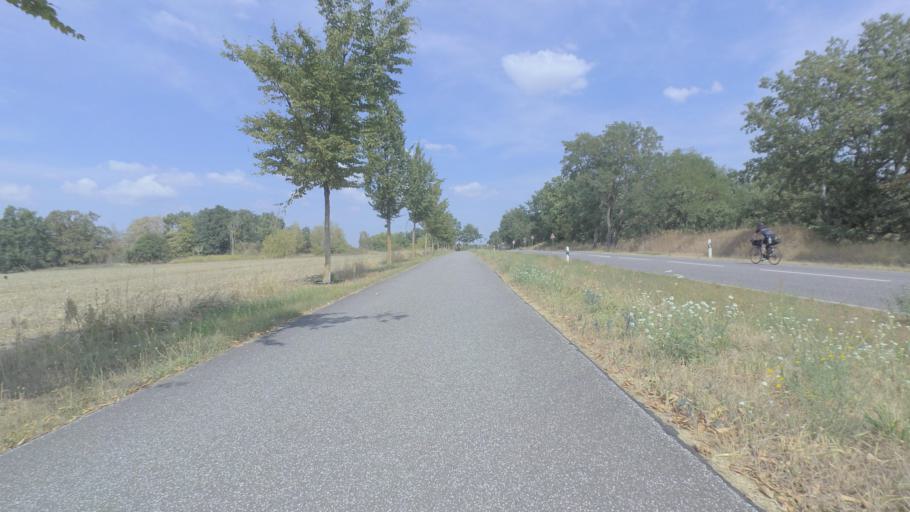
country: DE
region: Brandenburg
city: Wustermark
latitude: 52.5308
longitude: 12.9772
